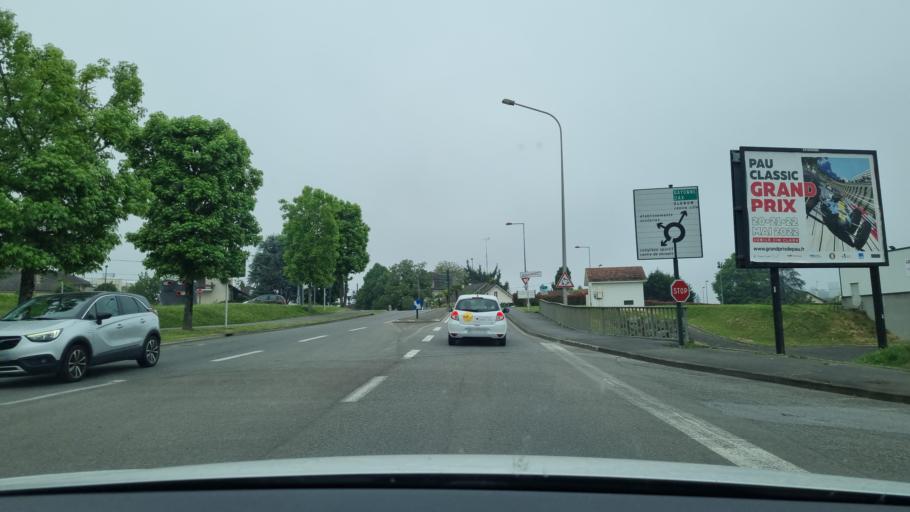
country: FR
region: Aquitaine
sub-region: Departement des Pyrenees-Atlantiques
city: Orthez
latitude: 43.4792
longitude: -0.7641
